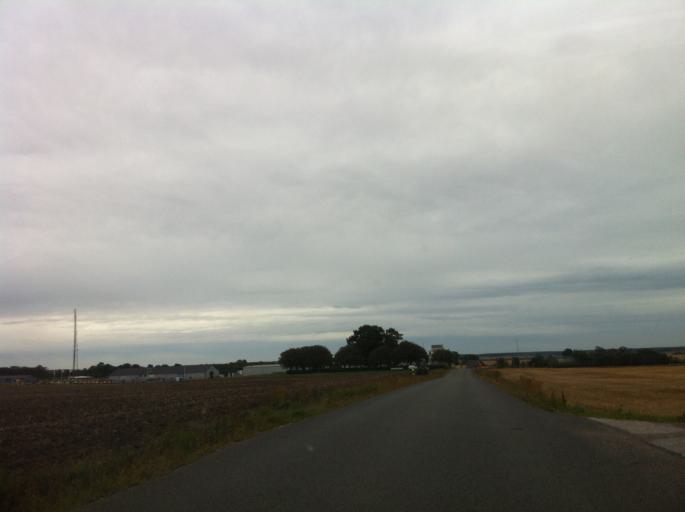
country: SE
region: Skane
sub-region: Landskrona
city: Asmundtorp
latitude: 55.8933
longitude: 12.9951
